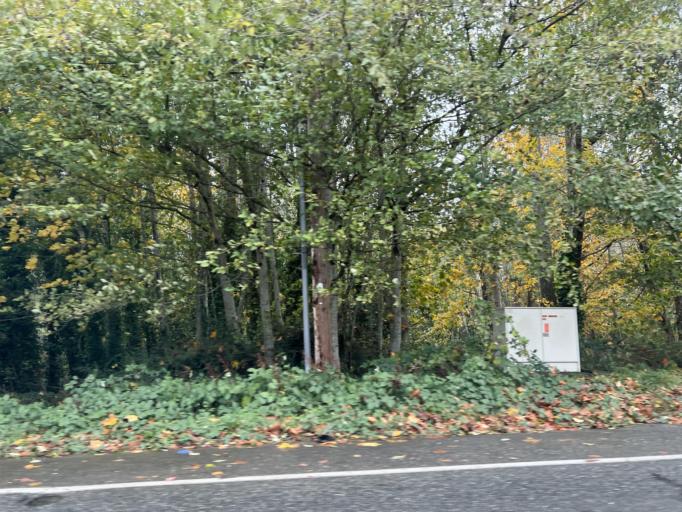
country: US
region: Washington
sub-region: Kitsap County
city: Bainbridge Island
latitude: 47.6377
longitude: -122.5210
